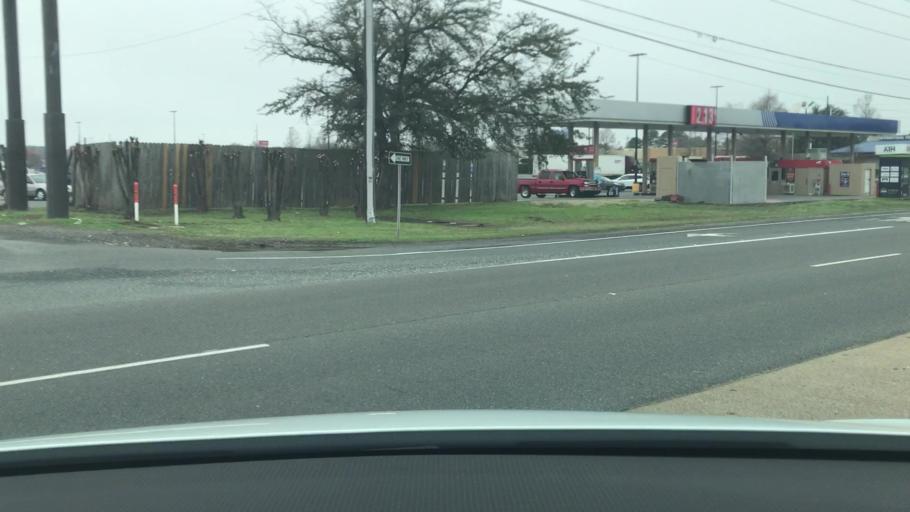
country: US
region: Louisiana
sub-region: Bossier Parish
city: Bossier City
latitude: 32.4297
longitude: -93.7107
